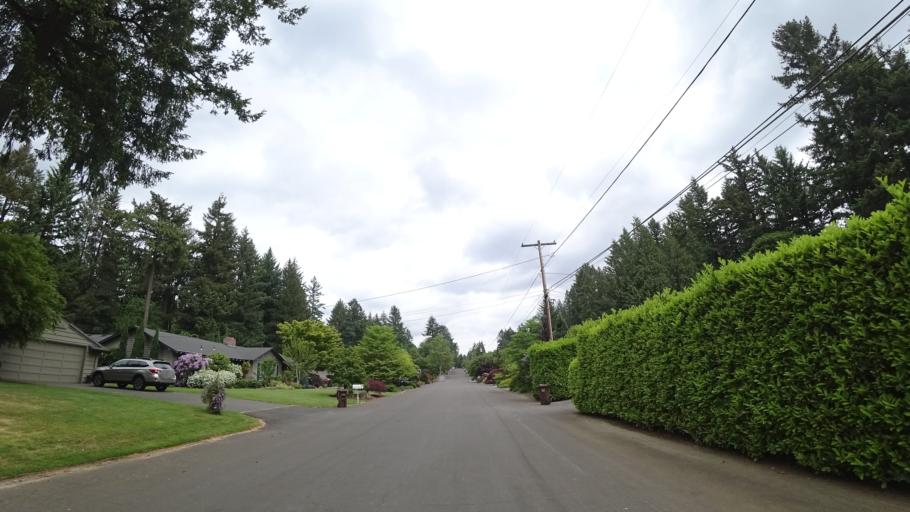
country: US
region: Oregon
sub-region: Washington County
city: Cedar Hills
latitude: 45.4991
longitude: -122.7847
